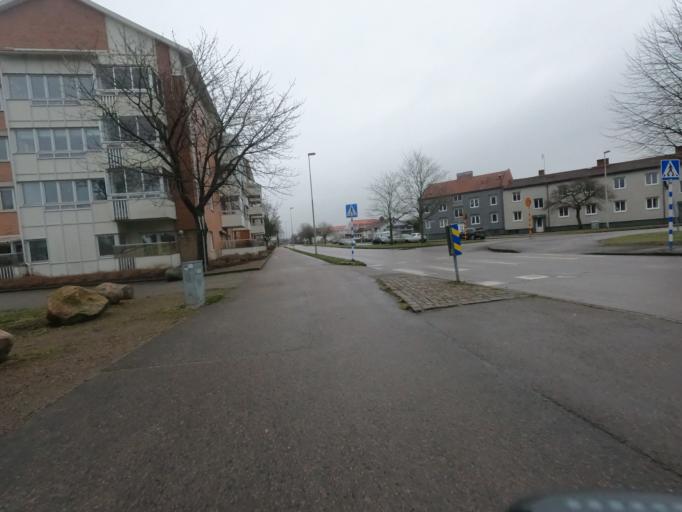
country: SE
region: Halland
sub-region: Halmstads Kommun
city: Halmstad
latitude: 56.6710
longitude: 12.8747
